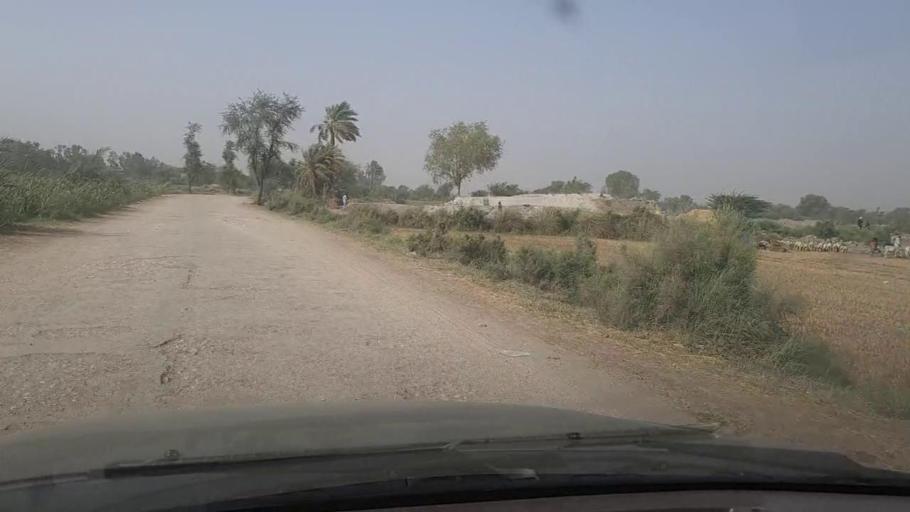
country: PK
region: Sindh
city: Shikarpur
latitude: 27.9157
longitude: 68.6080
